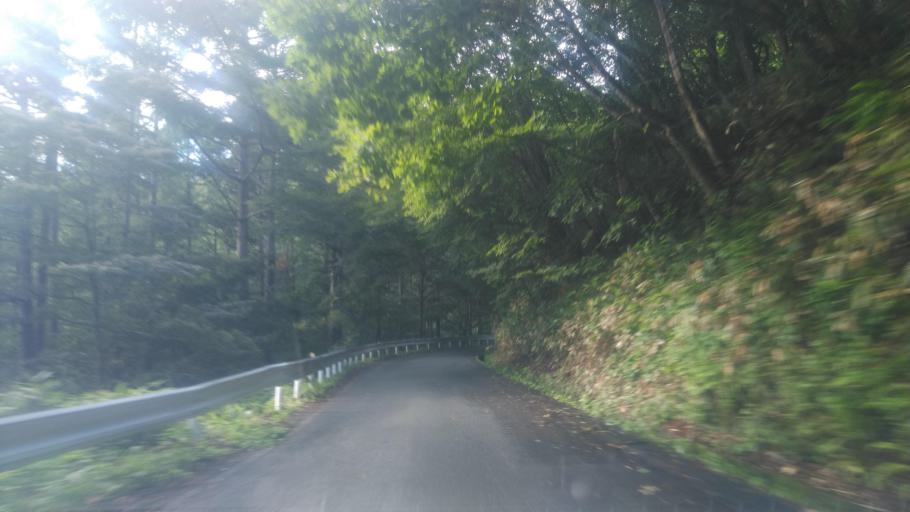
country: JP
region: Nagano
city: Ueda
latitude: 36.5033
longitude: 138.3770
